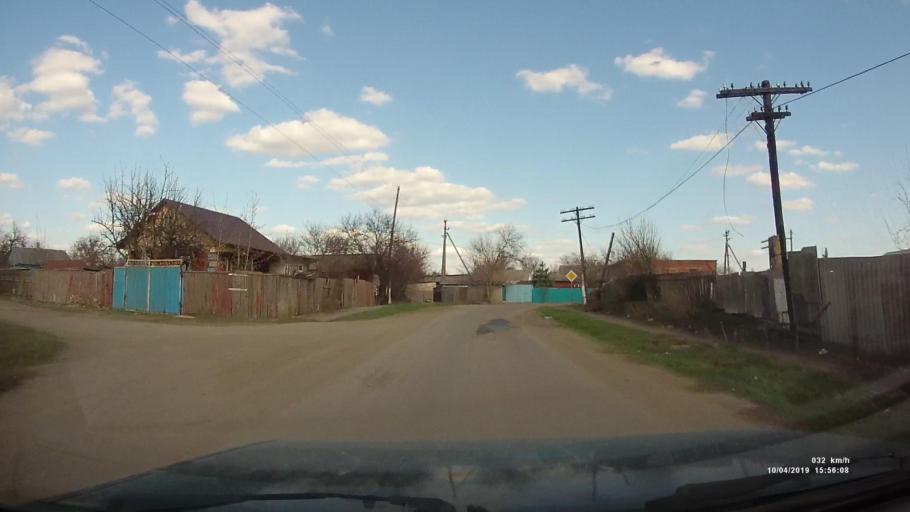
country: RU
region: Rostov
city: Masalovka
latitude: 48.4122
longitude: 40.2702
